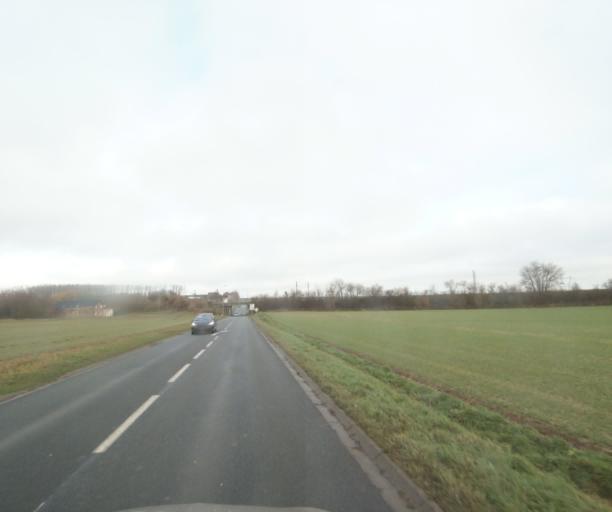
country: FR
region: Nord-Pas-de-Calais
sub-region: Departement du Nord
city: Famars
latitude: 50.2969
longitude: 3.5156
